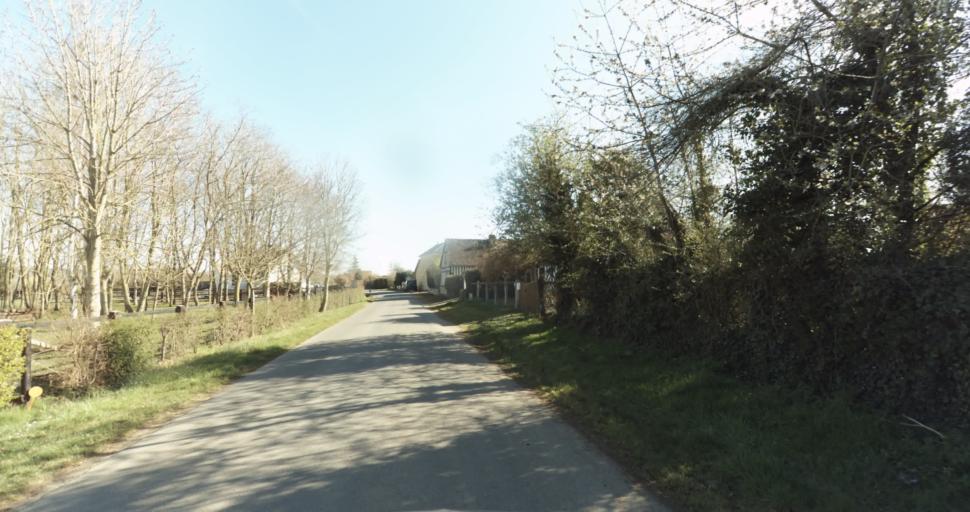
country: FR
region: Lower Normandy
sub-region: Departement du Calvados
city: Saint-Pierre-sur-Dives
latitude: 49.0364
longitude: 0.0519
